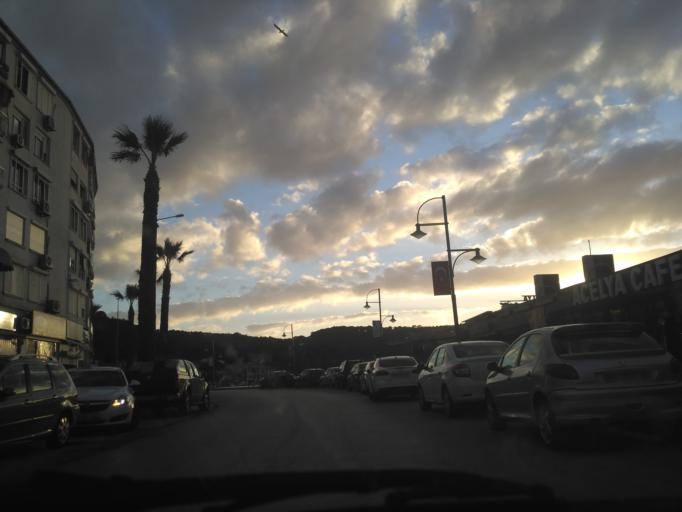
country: TR
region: Balikesir
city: Ayvalik
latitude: 39.3156
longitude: 26.6904
